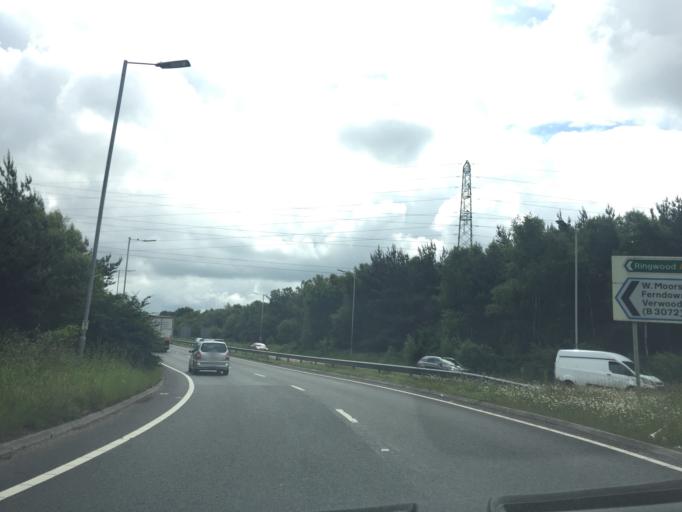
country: GB
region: England
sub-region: Dorset
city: Ferndown
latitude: 50.8186
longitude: -1.9059
